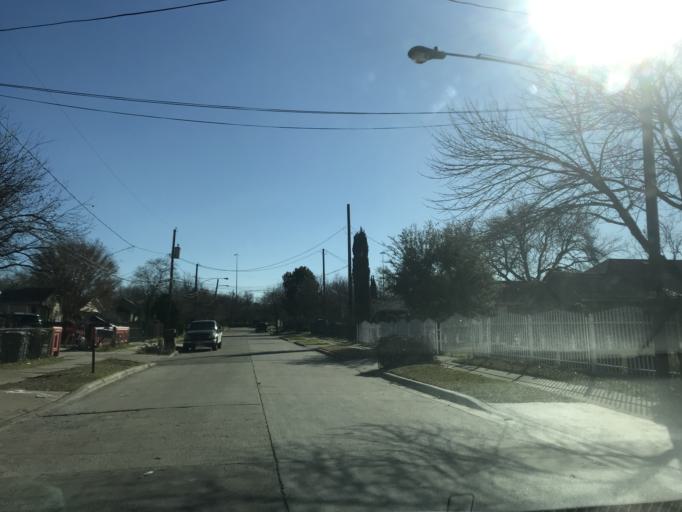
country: US
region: Texas
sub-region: Dallas County
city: Cockrell Hill
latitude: 32.7709
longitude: -96.9093
